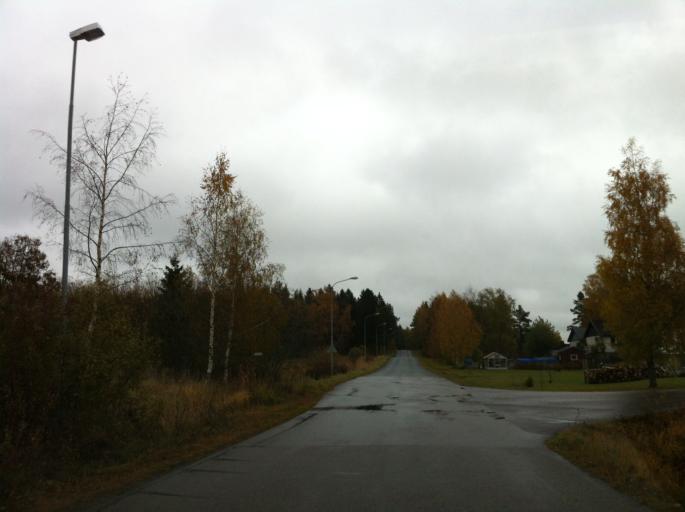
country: SE
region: Uppsala
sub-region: Osthammars Kommun
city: OEsthammar
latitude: 60.2667
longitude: 18.3516
